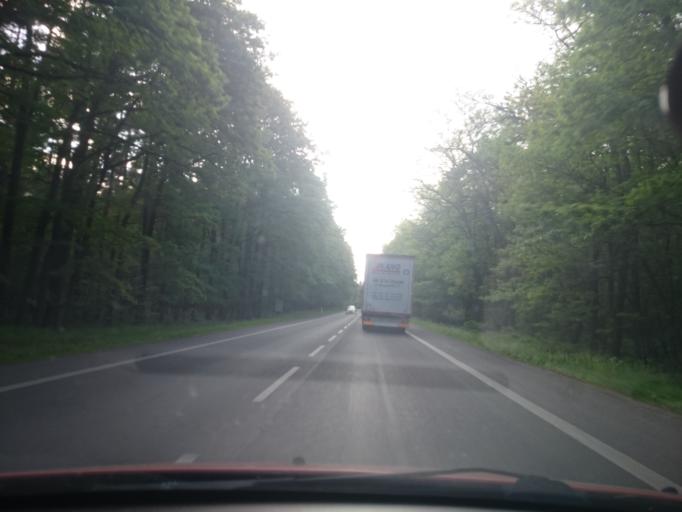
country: PL
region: Opole Voivodeship
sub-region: Powiat opolski
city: Chrzastowice
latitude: 50.6193
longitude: 18.0591
